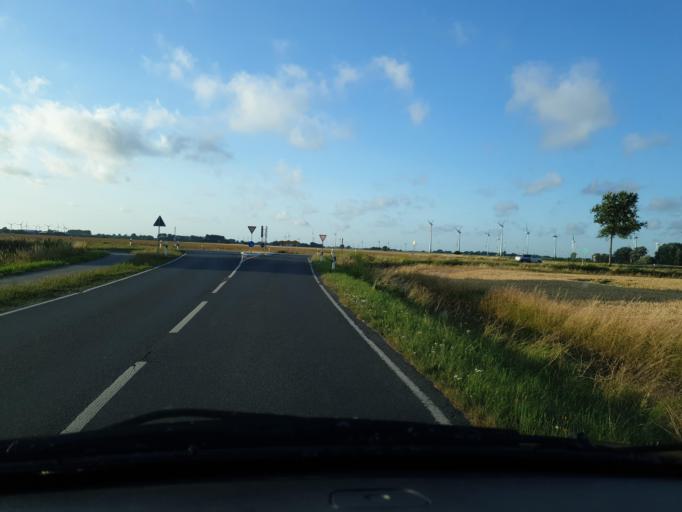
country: DE
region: Schleswig-Holstein
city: Wesselburener Deichhausen
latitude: 54.1509
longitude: 8.9176
